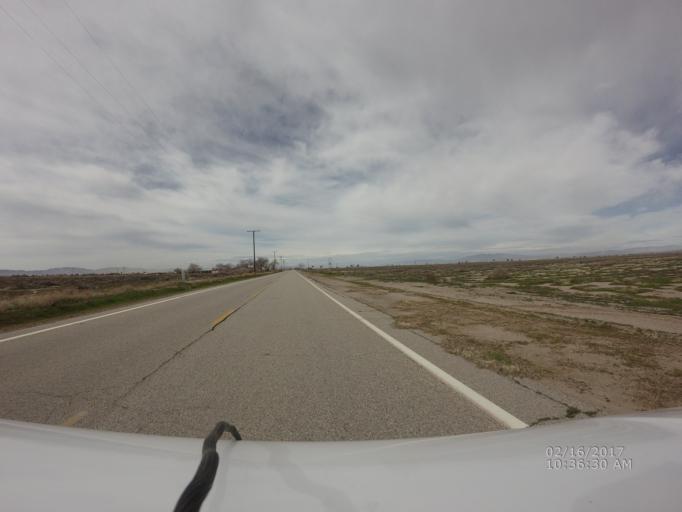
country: US
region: California
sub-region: Los Angeles County
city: Lancaster
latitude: 34.7195
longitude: -117.9839
